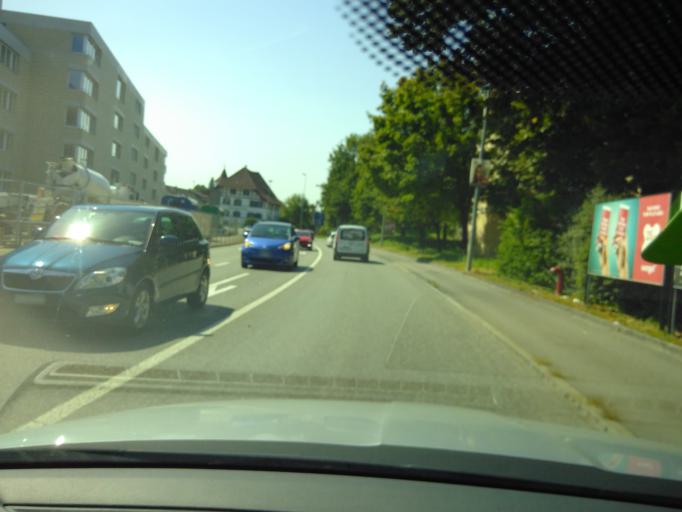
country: CH
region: Aargau
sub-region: Bezirk Aarau
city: Suhr
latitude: 47.3719
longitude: 8.0808
